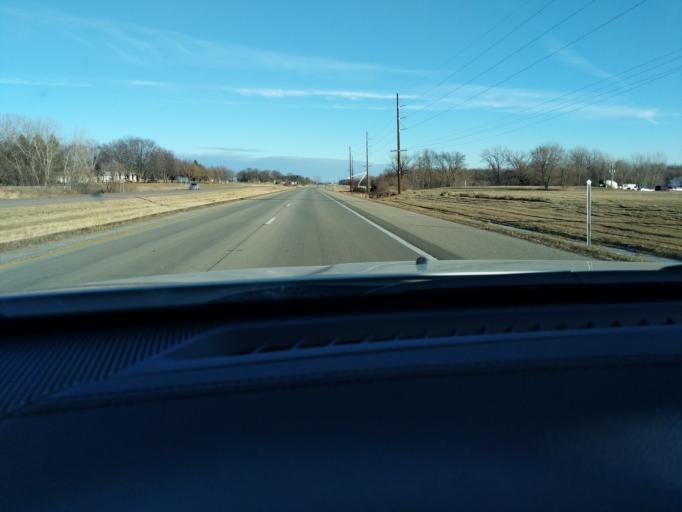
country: US
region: Minnesota
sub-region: McLeod County
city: Glencoe
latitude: 44.7688
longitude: -94.1213
